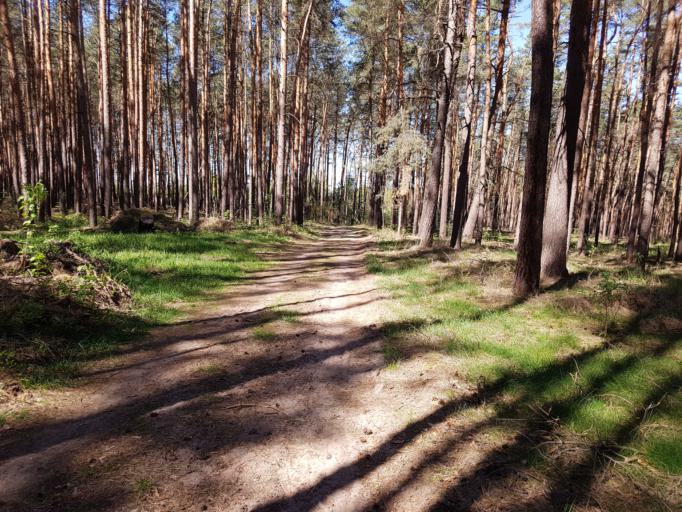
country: DE
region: Brandenburg
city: Groden
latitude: 51.3914
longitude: 13.5743
